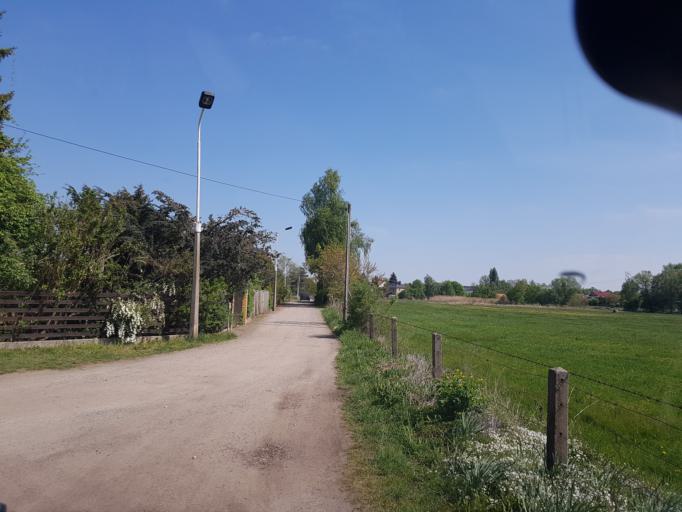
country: DE
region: Brandenburg
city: Finsterwalde
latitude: 51.6217
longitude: 13.7004
